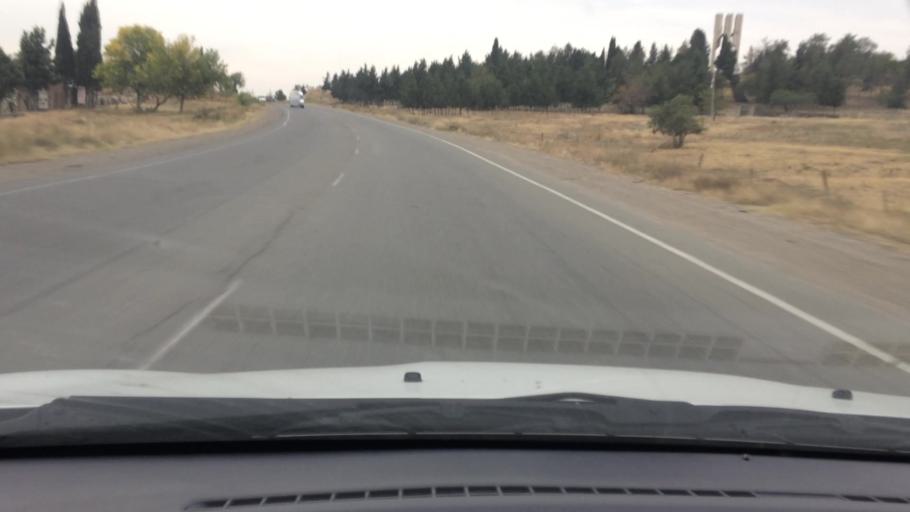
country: GE
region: Kvemo Kartli
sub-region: Marneuli
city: Marneuli
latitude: 41.5263
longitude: 44.7771
